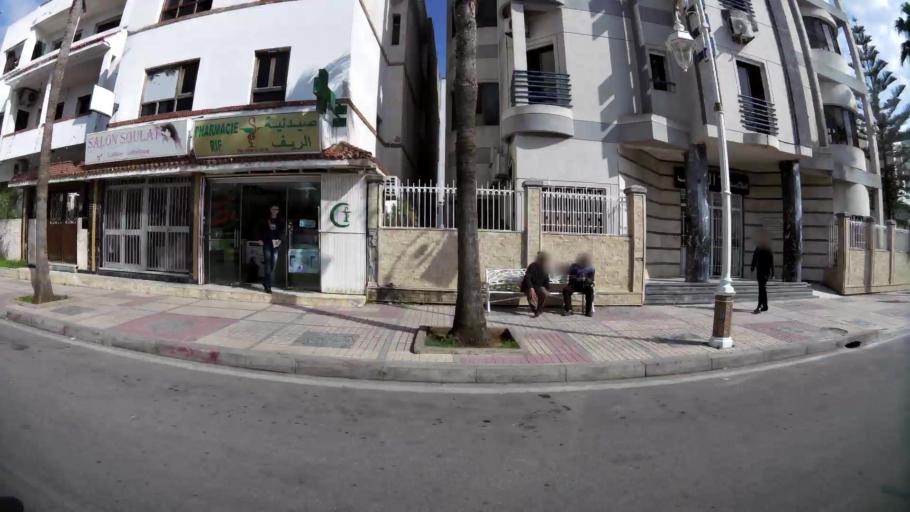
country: MA
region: Tanger-Tetouan
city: Tetouan
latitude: 35.5869
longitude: -5.3470
